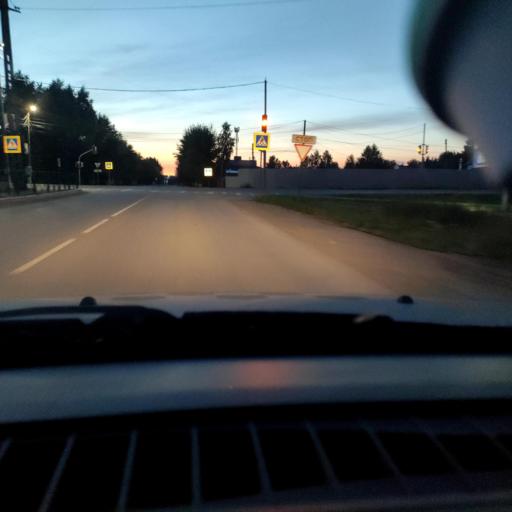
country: RU
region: Perm
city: Polazna
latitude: 58.2929
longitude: 56.4006
